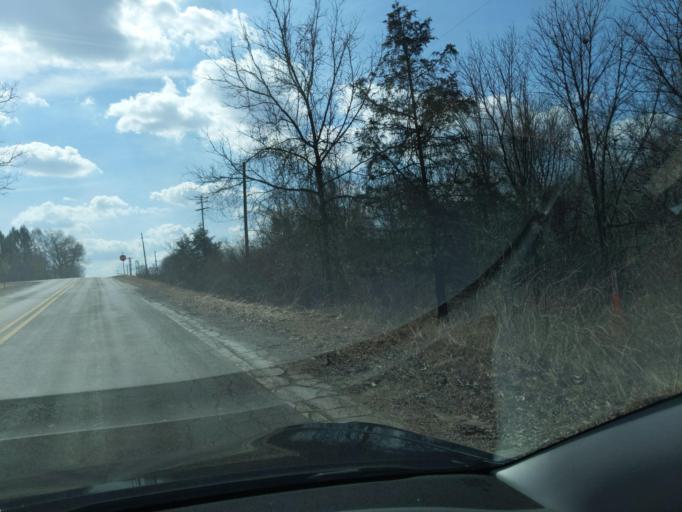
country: US
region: Michigan
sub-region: Washtenaw County
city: Chelsea
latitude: 42.3841
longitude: -84.0155
